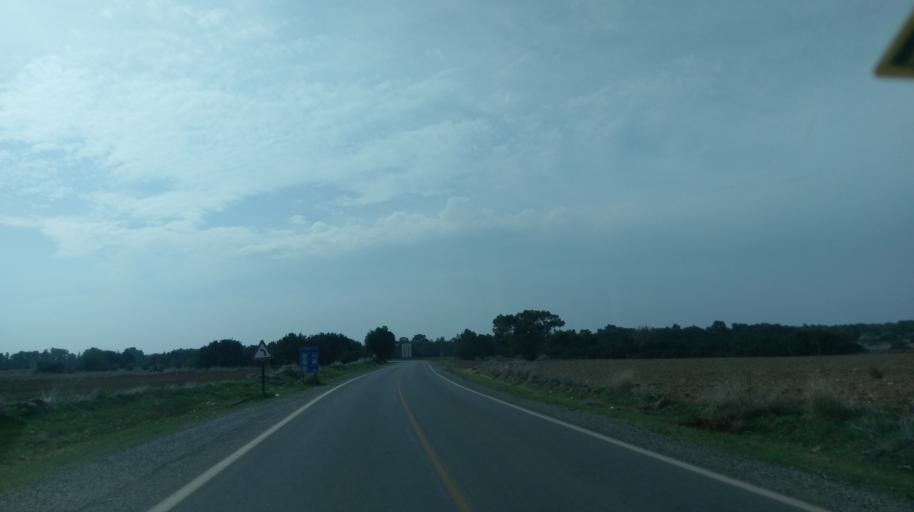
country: CY
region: Lefkosia
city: Morfou
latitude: 35.2957
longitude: 33.0437
